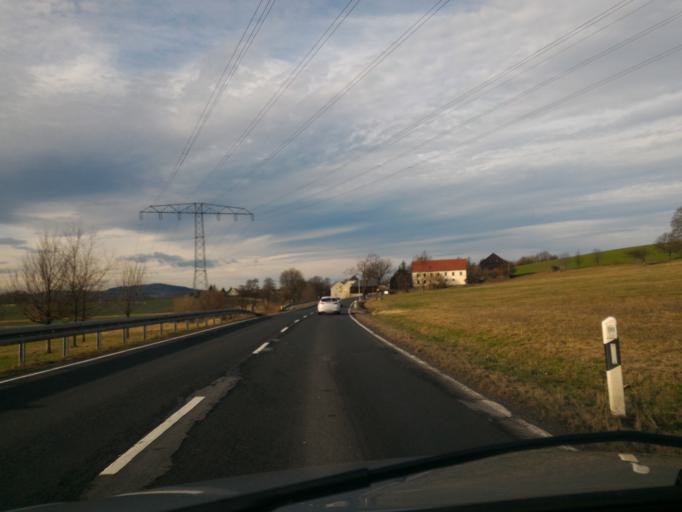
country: DE
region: Saxony
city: Neukirch/Lausitz
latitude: 51.0974
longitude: 14.2695
